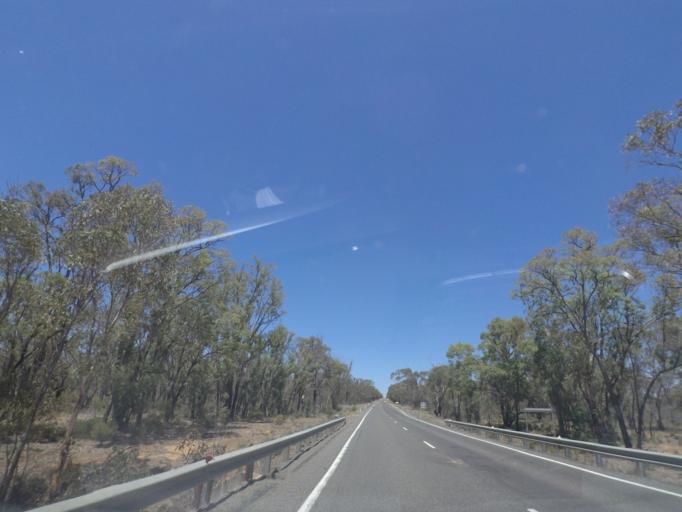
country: AU
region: New South Wales
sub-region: Narrabri
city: Narrabri
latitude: -30.7210
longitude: 149.5254
